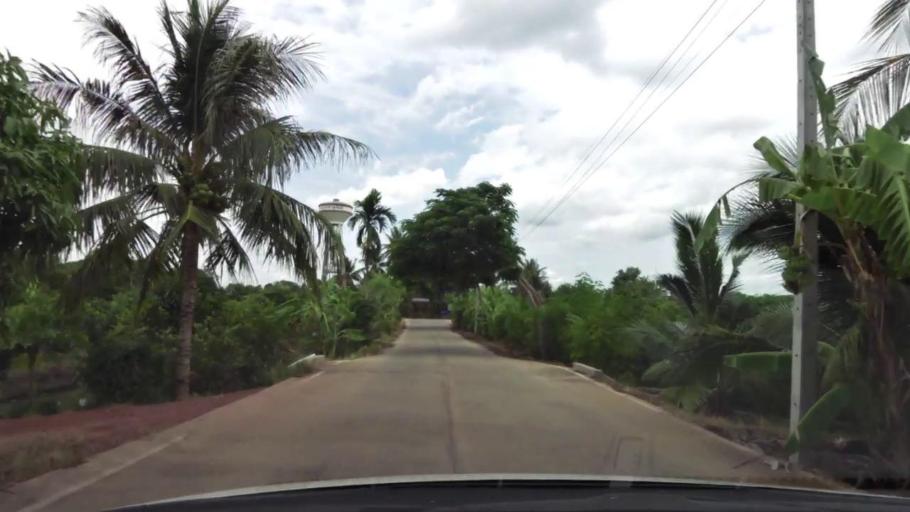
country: TH
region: Samut Sakhon
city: Ban Phaeo
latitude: 13.5664
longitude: 100.0357
